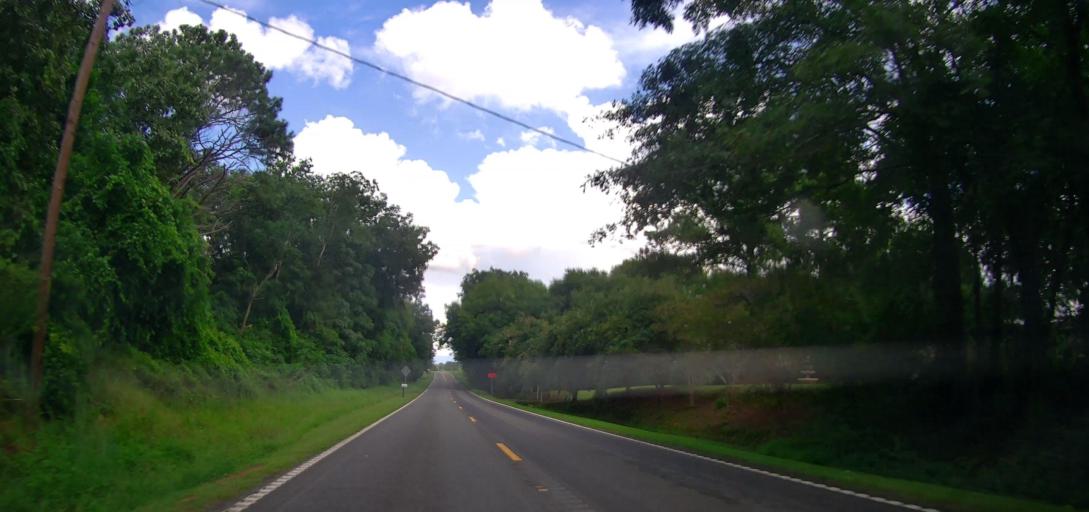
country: US
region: Georgia
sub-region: Taylor County
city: Reynolds
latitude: 32.4402
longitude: -84.1272
